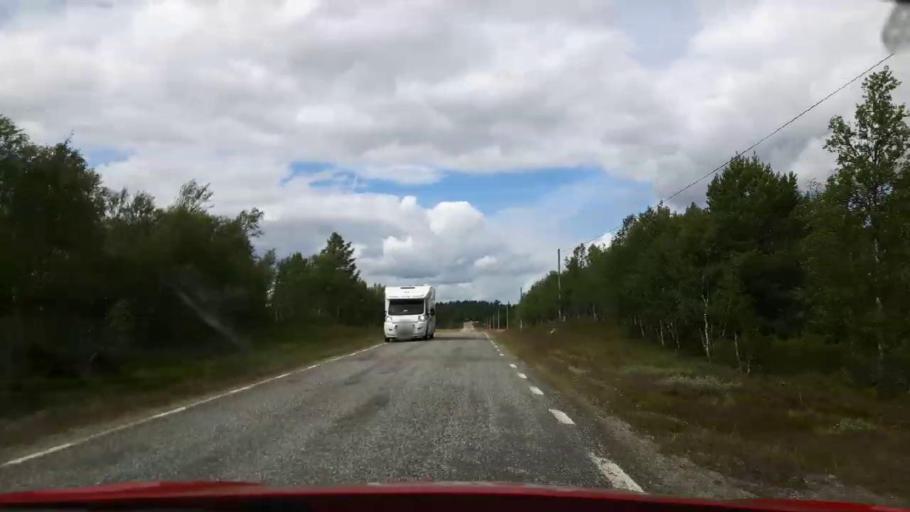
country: NO
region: Hedmark
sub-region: Engerdal
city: Engerdal
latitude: 62.2936
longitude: 12.8128
